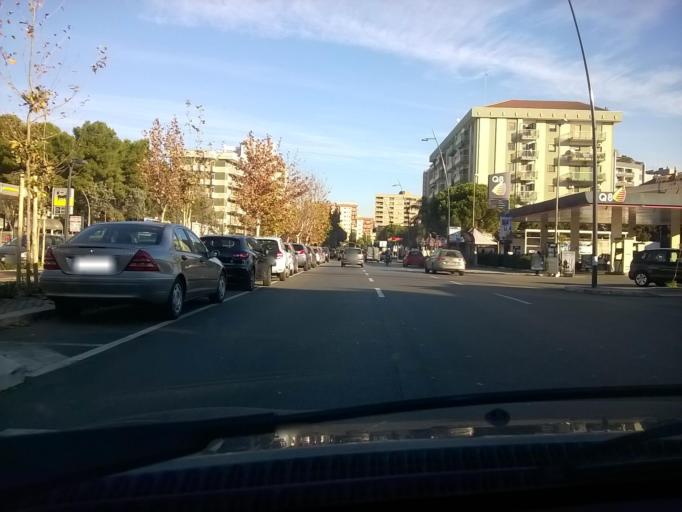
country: IT
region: Apulia
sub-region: Provincia di Taranto
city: Taranto
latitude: 40.4595
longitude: 17.2676
